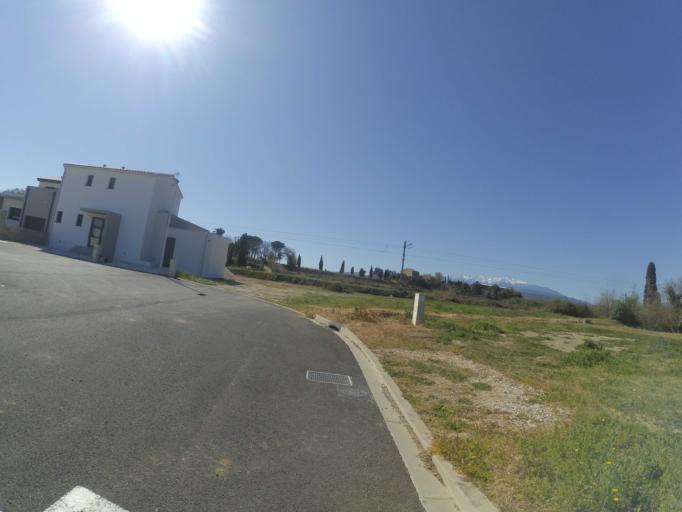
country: FR
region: Languedoc-Roussillon
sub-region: Departement des Pyrenees-Orientales
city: Corneilla-la-Riviere
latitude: 42.6824
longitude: 2.7185
